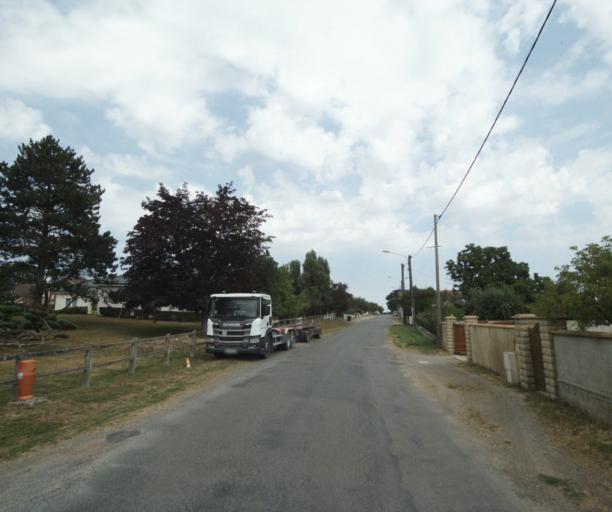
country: FR
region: Bourgogne
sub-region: Departement de Saone-et-Loire
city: Gueugnon
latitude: 46.5931
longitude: 4.0419
